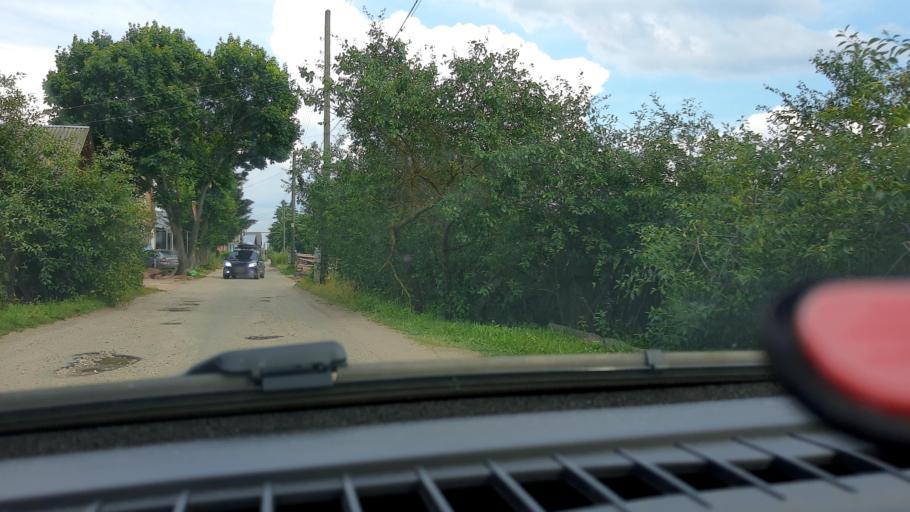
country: RU
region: Nizjnij Novgorod
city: Gorodets
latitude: 56.6173
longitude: 43.4951
